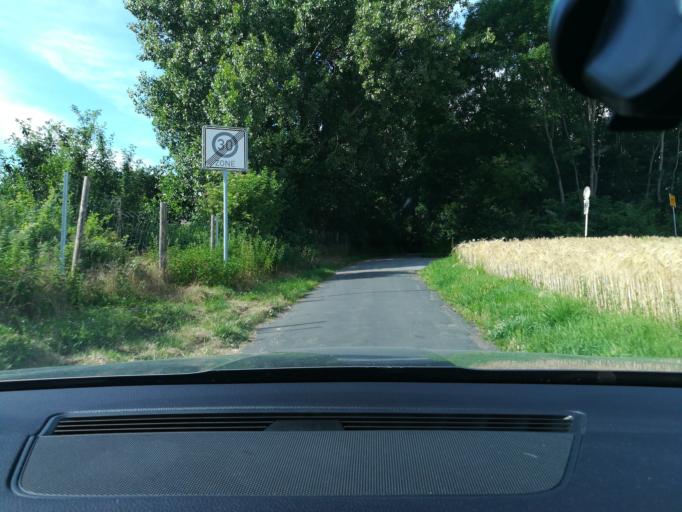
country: DE
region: North Rhine-Westphalia
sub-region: Regierungsbezirk Detmold
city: Minden
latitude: 52.3117
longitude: 8.9440
